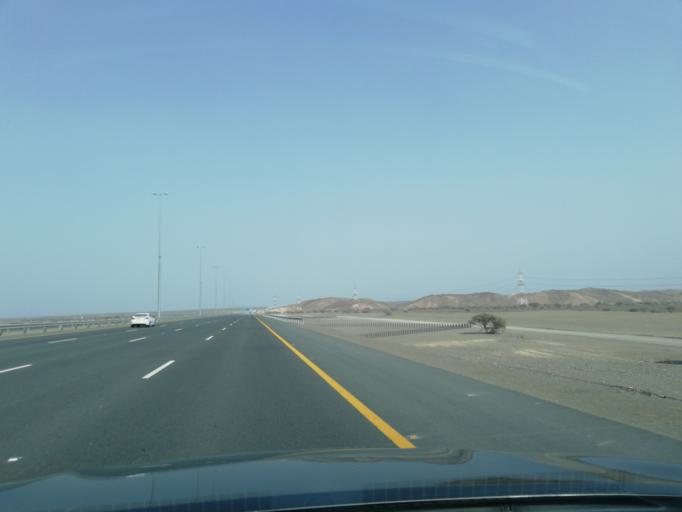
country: OM
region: Al Batinah
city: Al Sohar
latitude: 24.3045
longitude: 56.5969
